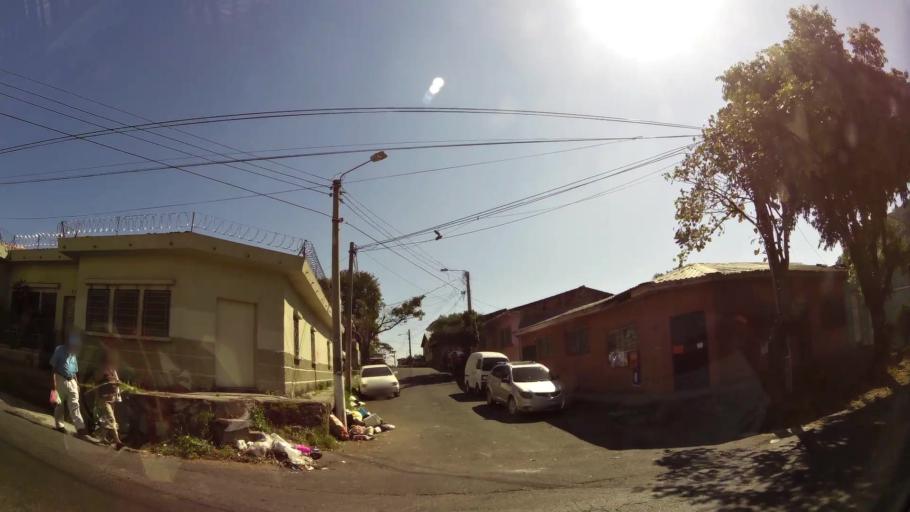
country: SV
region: La Libertad
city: Santa Tecla
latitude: 13.6691
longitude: -89.2849
